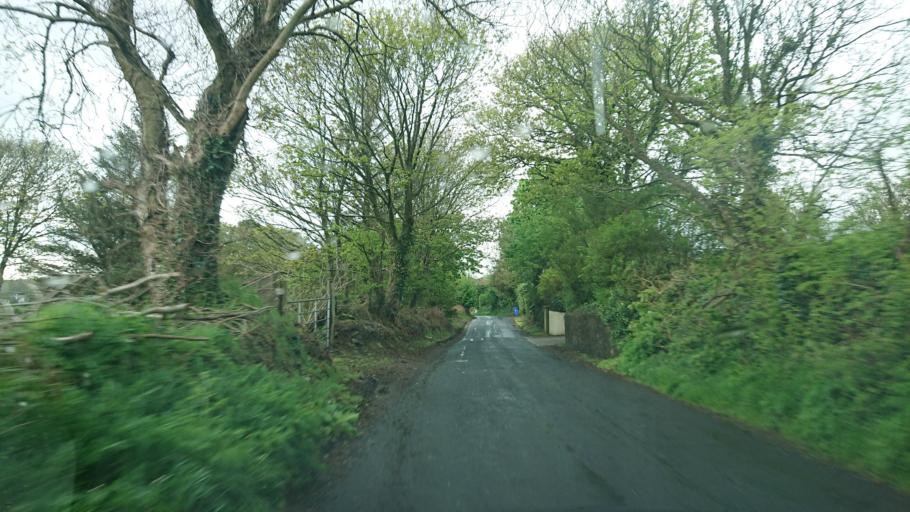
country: IE
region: Munster
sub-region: Waterford
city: Waterford
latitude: 52.2286
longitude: -7.0727
